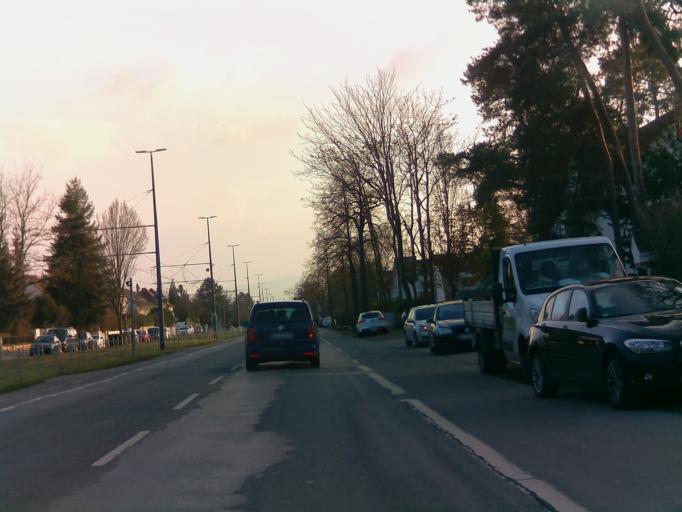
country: DE
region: Hesse
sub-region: Regierungsbezirk Darmstadt
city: Darmstadt
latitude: 49.8312
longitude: 8.6449
